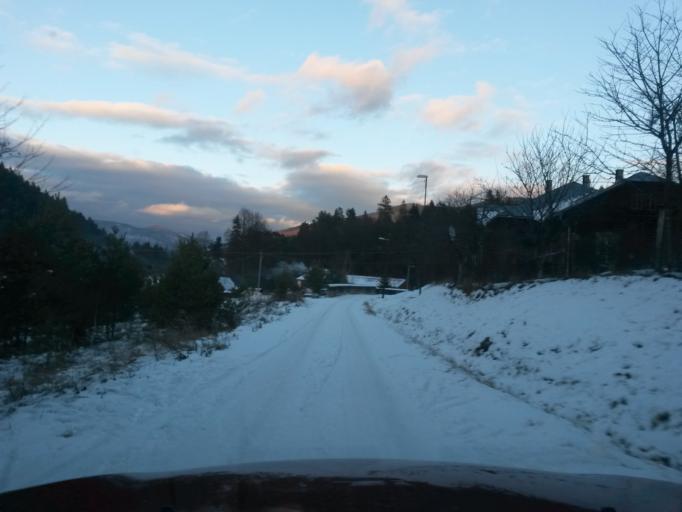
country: SK
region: Kosicky
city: Medzev
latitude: 48.7834
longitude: 20.7981
